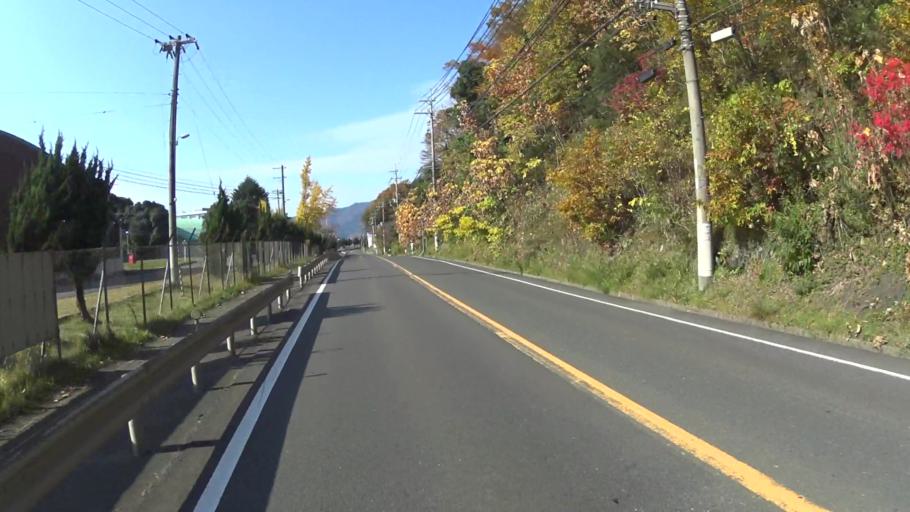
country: JP
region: Kyoto
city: Maizuru
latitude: 35.4860
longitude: 135.3994
